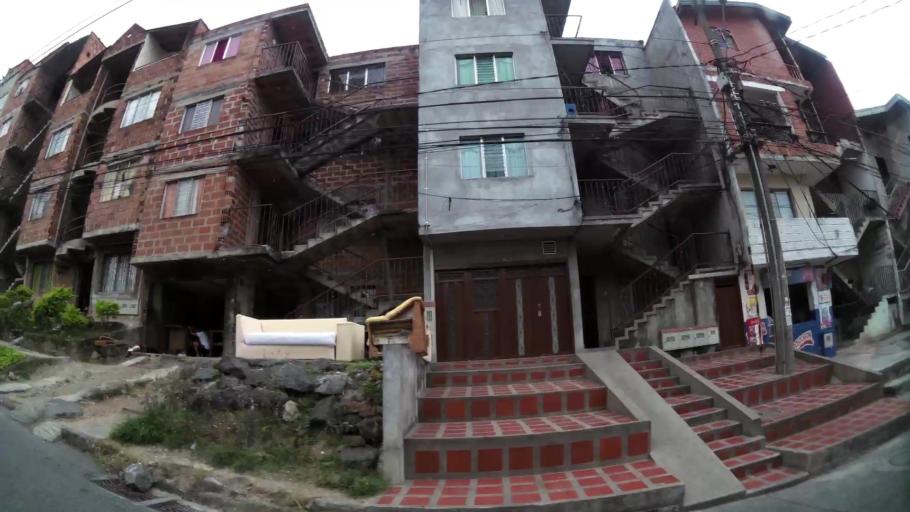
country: CO
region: Antioquia
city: Medellin
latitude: 6.2328
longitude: -75.5540
